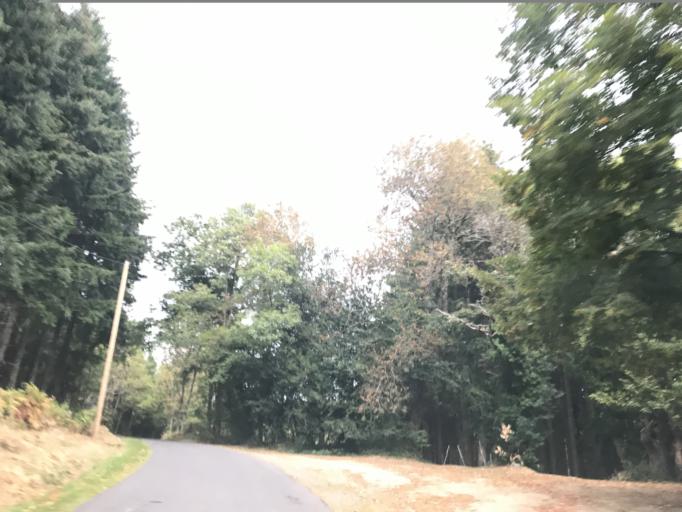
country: FR
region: Auvergne
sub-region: Departement du Puy-de-Dome
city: Thiers
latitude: 45.8378
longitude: 3.5840
